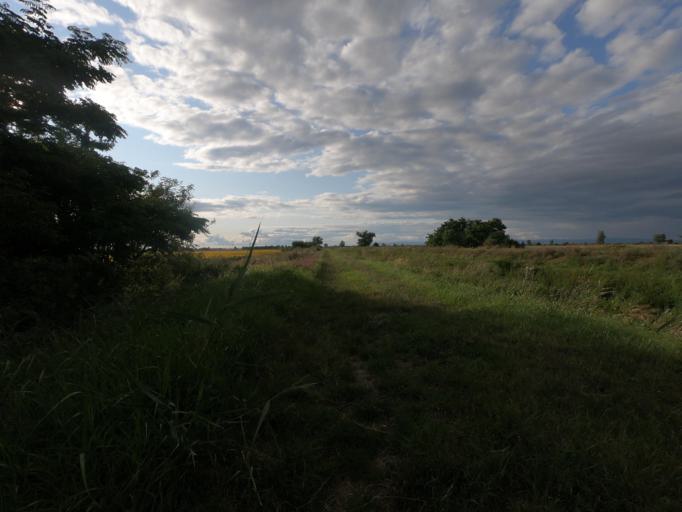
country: HU
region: Heves
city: Poroszlo
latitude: 47.7069
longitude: 20.5812
